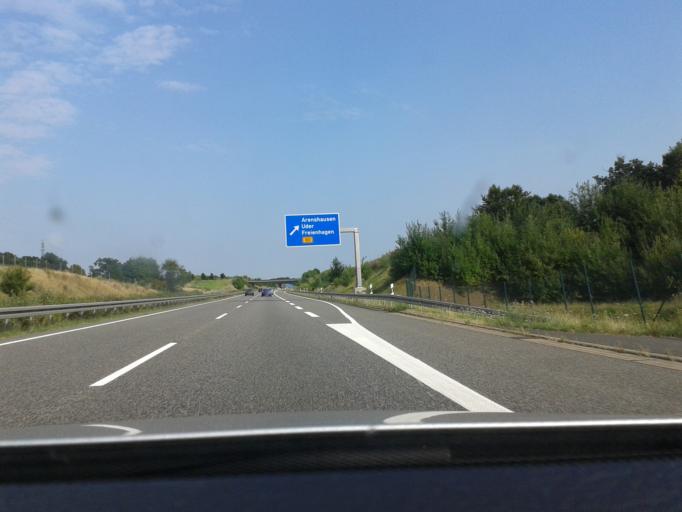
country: DE
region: Thuringia
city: Schachtebich
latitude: 51.3993
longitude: 10.0296
